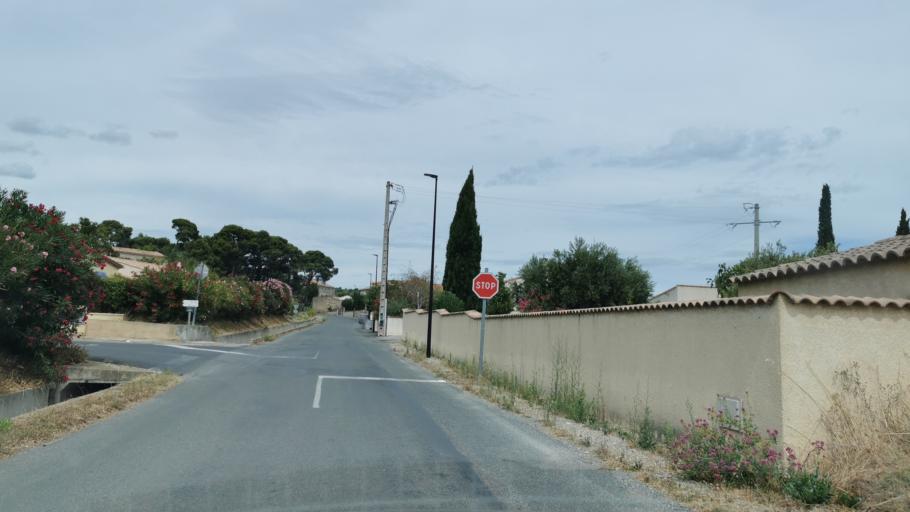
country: FR
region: Languedoc-Roussillon
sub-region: Departement de l'Aude
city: Bize-Minervois
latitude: 43.3000
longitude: 2.8278
